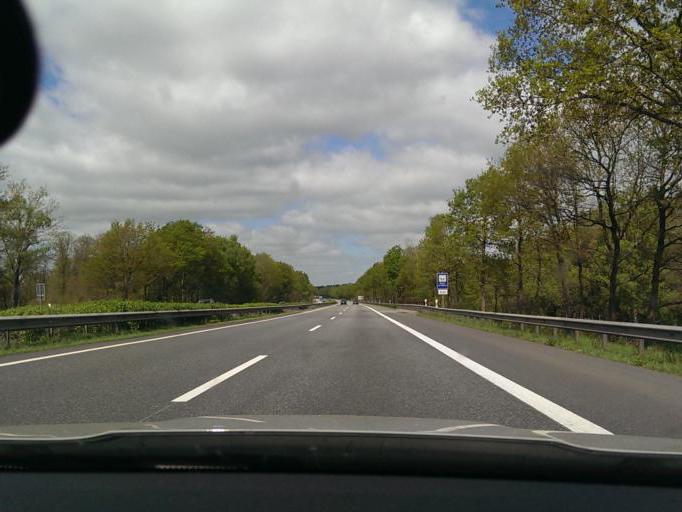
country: DE
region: Lower Saxony
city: Kirchlinteln
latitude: 52.9212
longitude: 9.3495
